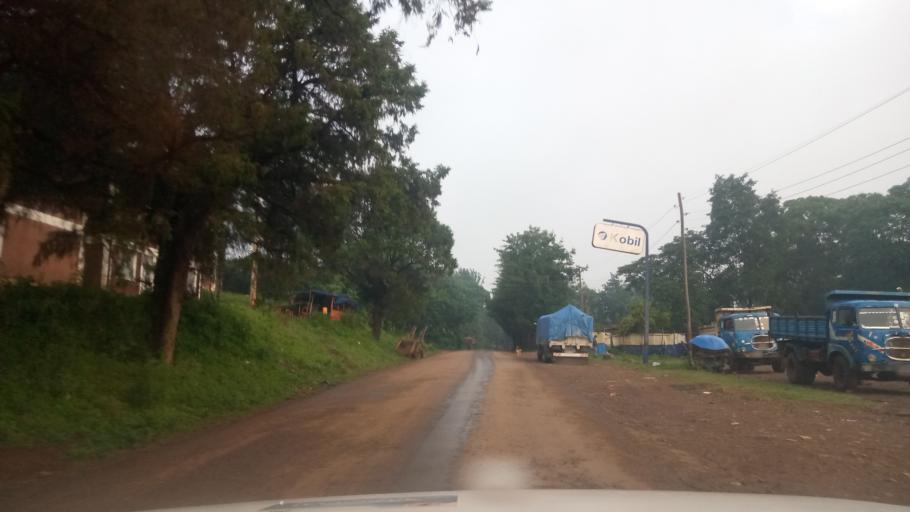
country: ET
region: Oromiya
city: Jima
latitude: 7.6875
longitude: 36.8292
